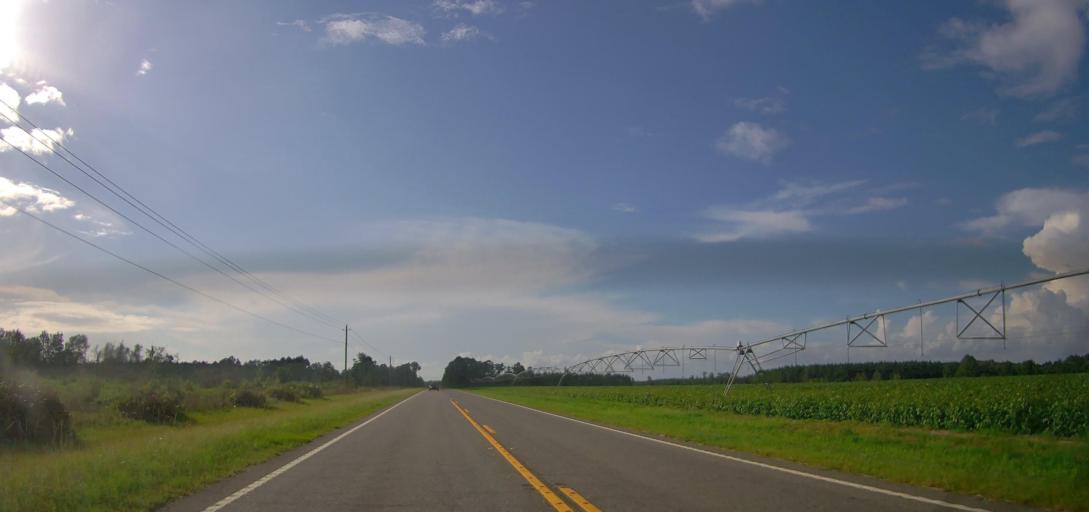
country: US
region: Georgia
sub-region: Coffee County
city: Nicholls
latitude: 31.3502
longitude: -82.6143
